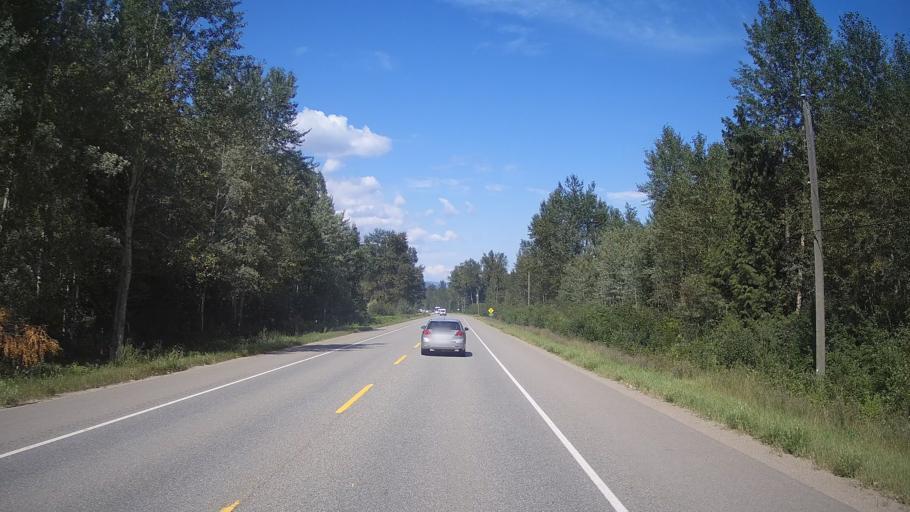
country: CA
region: British Columbia
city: Chase
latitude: 51.4927
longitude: -120.1786
